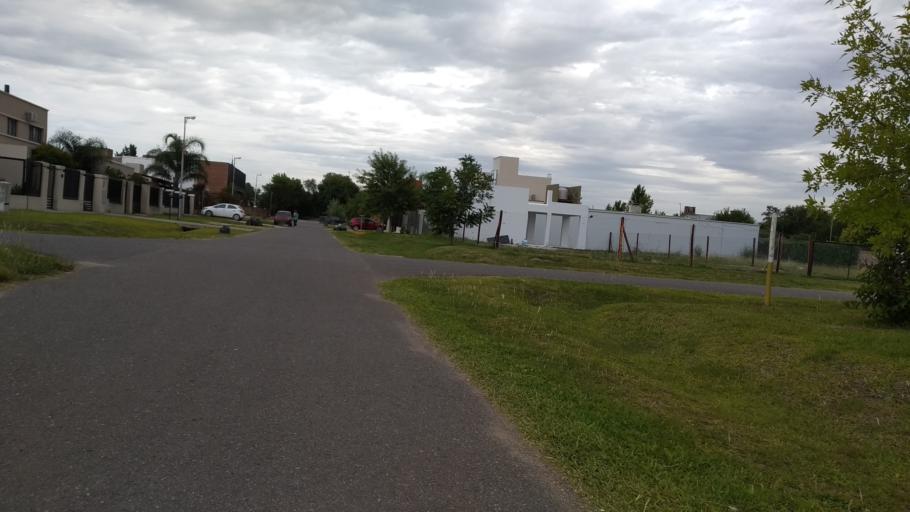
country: AR
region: Santa Fe
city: Funes
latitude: -32.9304
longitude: -60.8037
